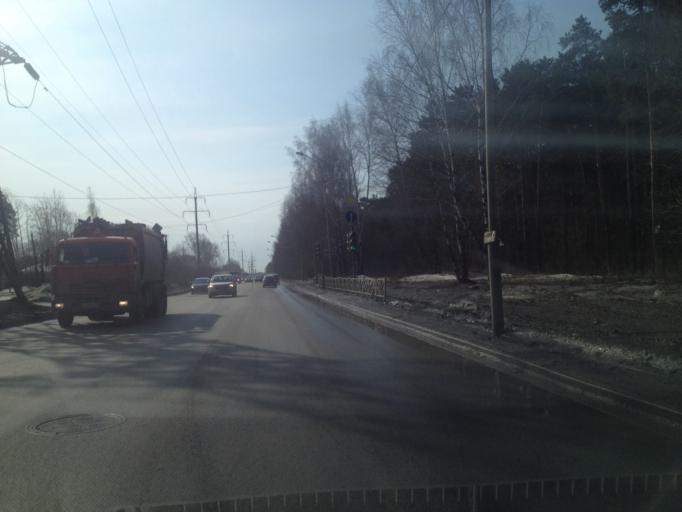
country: RU
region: Sverdlovsk
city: Sovkhoznyy
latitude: 56.7845
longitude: 60.5980
